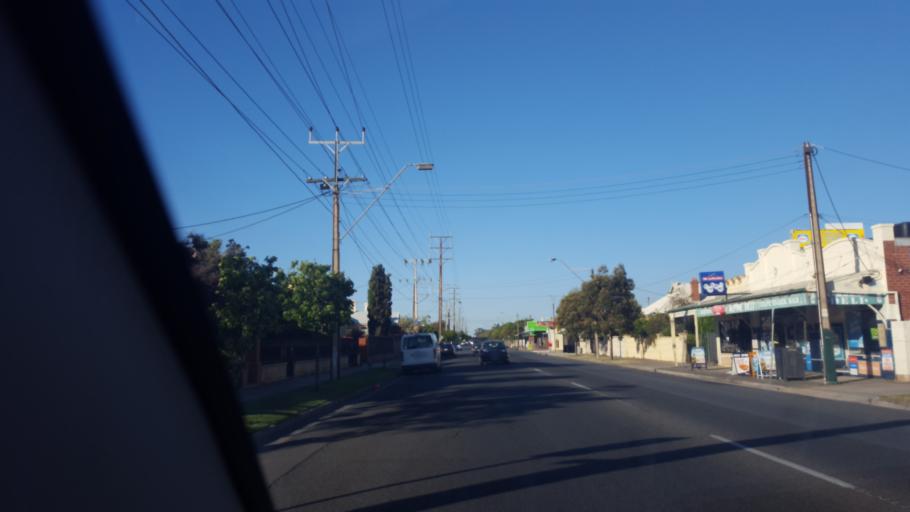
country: AU
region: South Australia
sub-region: Port Adelaide Enfield
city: Birkenhead
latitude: -34.8298
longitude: 138.4878
